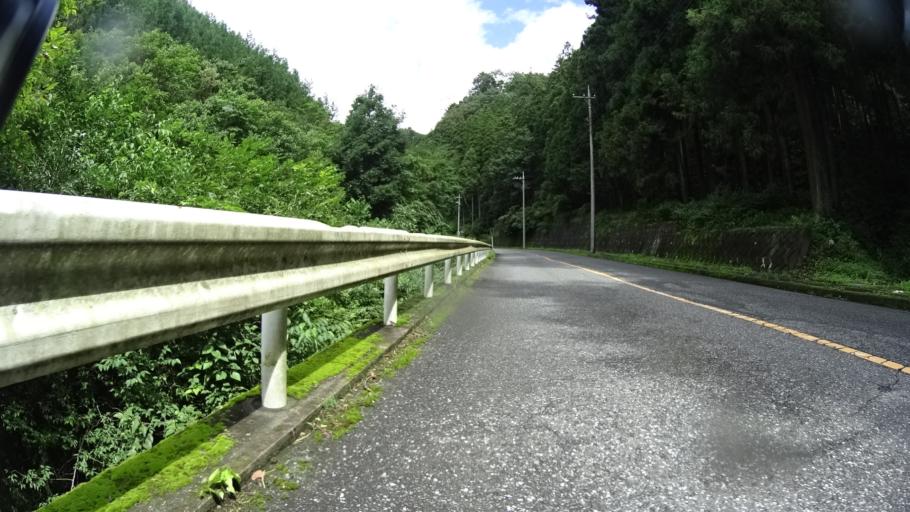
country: JP
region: Tokyo
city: Ome
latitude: 35.8296
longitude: 139.2145
